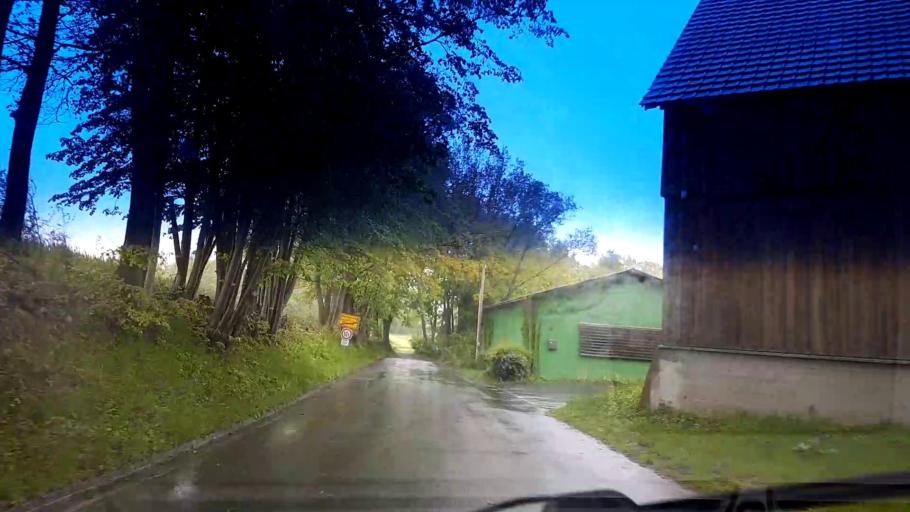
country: DE
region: Bavaria
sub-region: Upper Franconia
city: Bindlach
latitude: 50.0148
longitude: 11.6255
